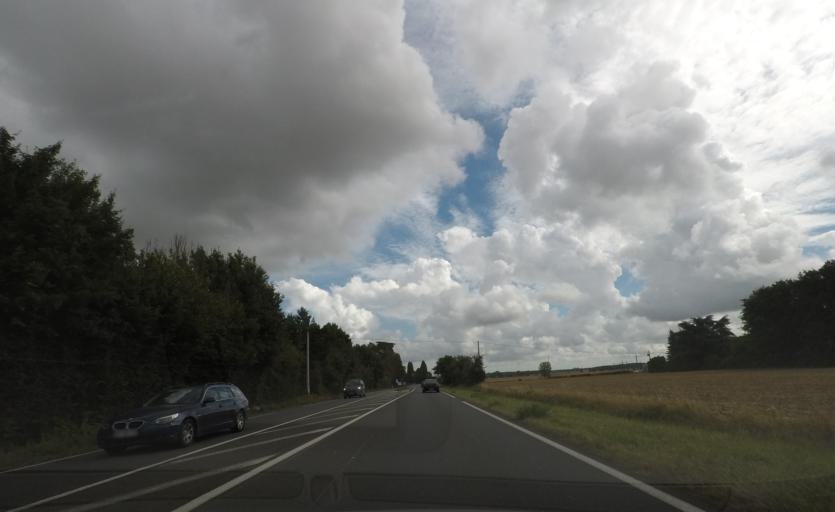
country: FR
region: Pays de la Loire
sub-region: Departement de Maine-et-Loire
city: Pellouailles-les-Vignes
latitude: 47.5328
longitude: -0.4158
